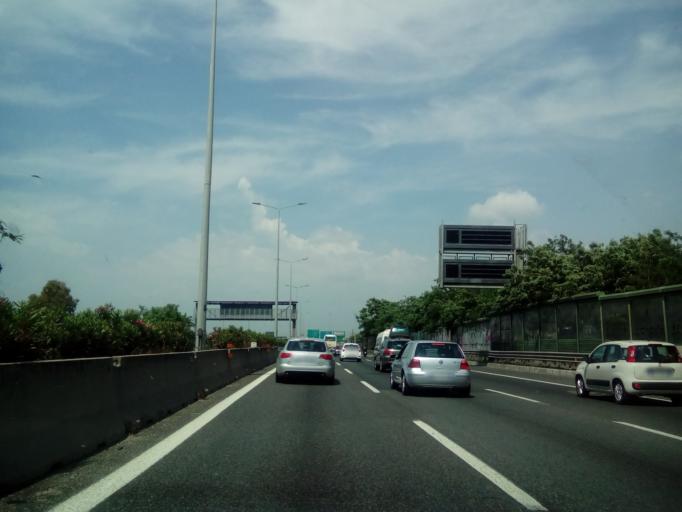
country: IT
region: Latium
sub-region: Citta metropolitana di Roma Capitale
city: Ciampino
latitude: 41.8171
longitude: 12.5769
